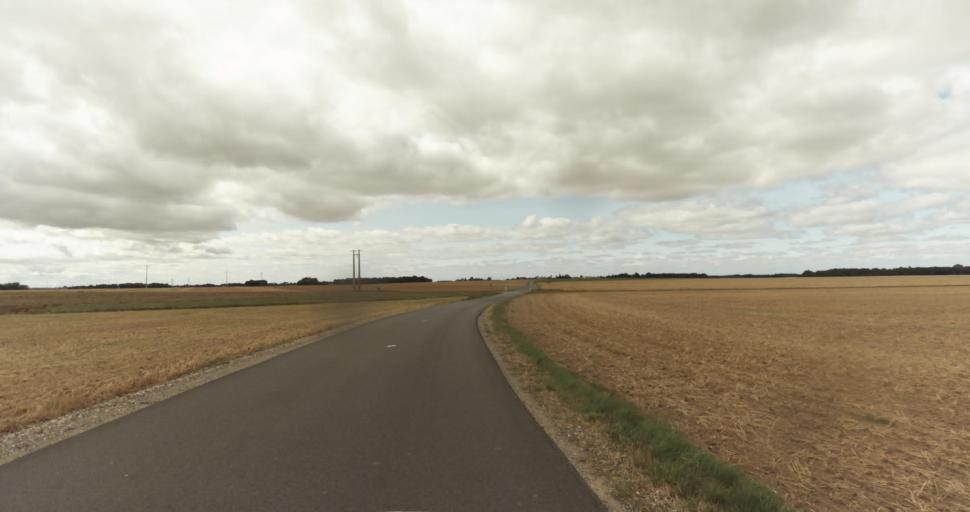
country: FR
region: Haute-Normandie
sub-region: Departement de l'Eure
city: Marcilly-sur-Eure
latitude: 48.9106
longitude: 1.2422
